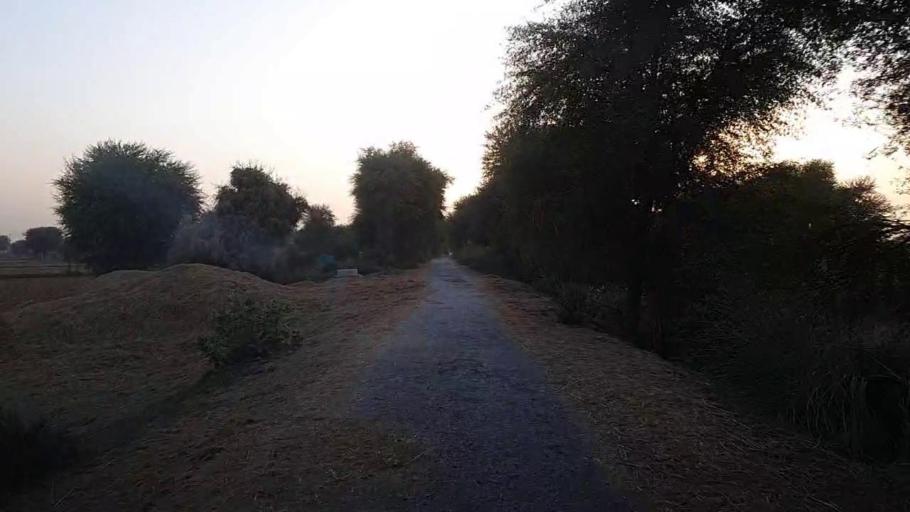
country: PK
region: Sindh
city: Kashmor
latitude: 28.4148
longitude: 69.4475
